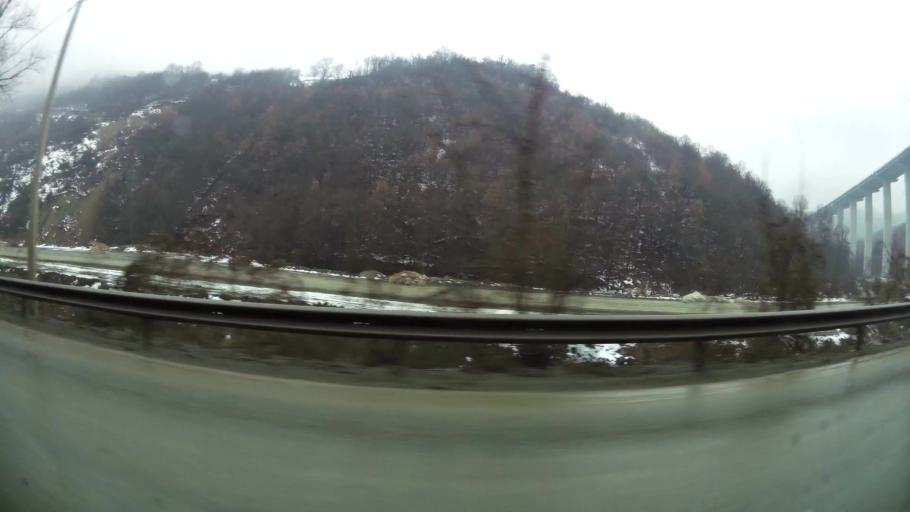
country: XK
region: Ferizaj
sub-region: Hani i Elezit
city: Hani i Elezit
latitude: 42.1677
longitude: 21.2776
